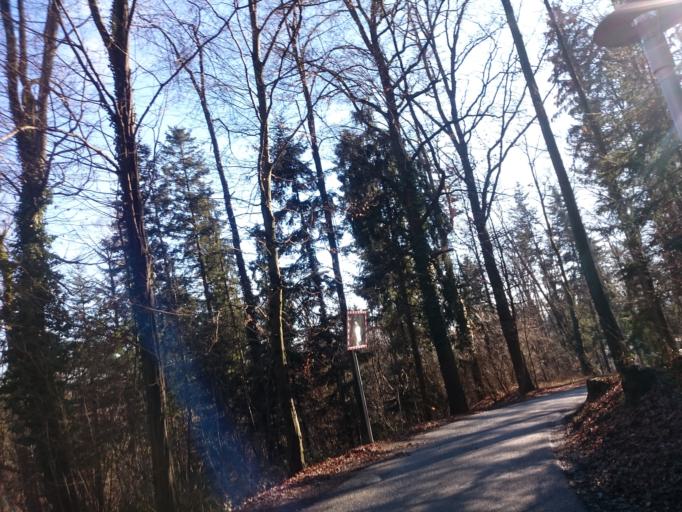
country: AT
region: Styria
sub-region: Graz Stadt
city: Graz
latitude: 47.0884
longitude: 15.4694
